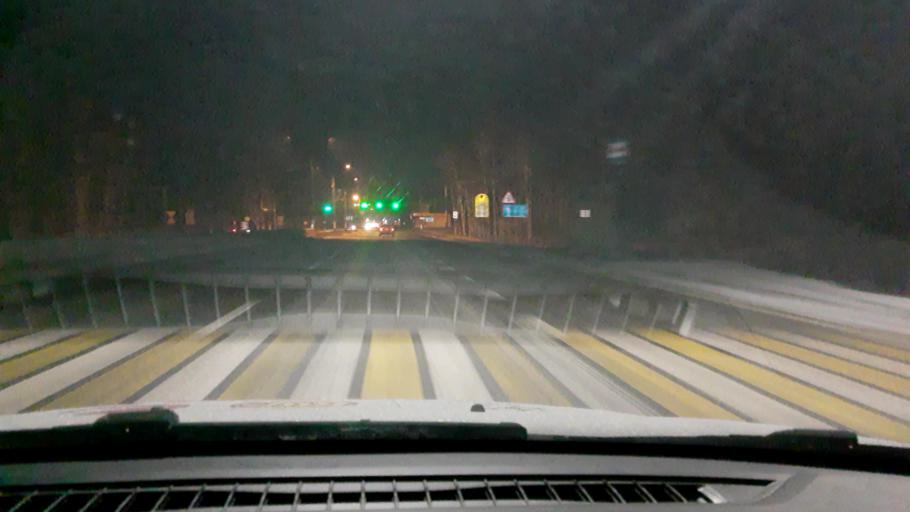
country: RU
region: Nizjnij Novgorod
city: Dzerzhinsk
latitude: 56.2986
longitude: 43.4800
